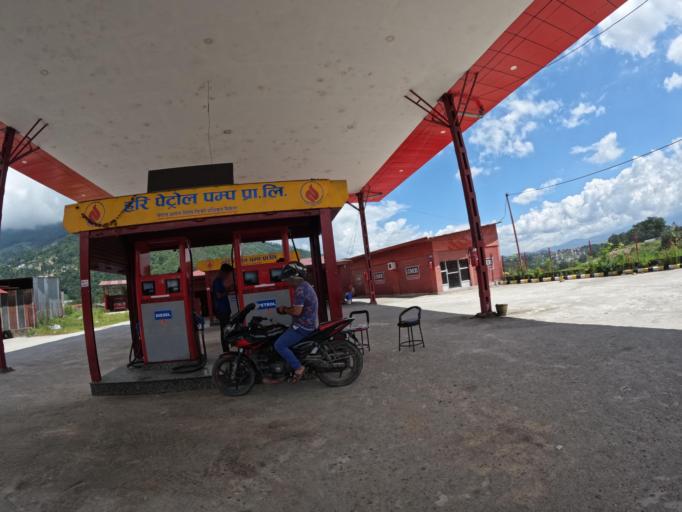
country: NP
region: Central Region
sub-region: Bagmati Zone
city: Kathmandu
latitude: 27.7817
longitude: 85.3252
